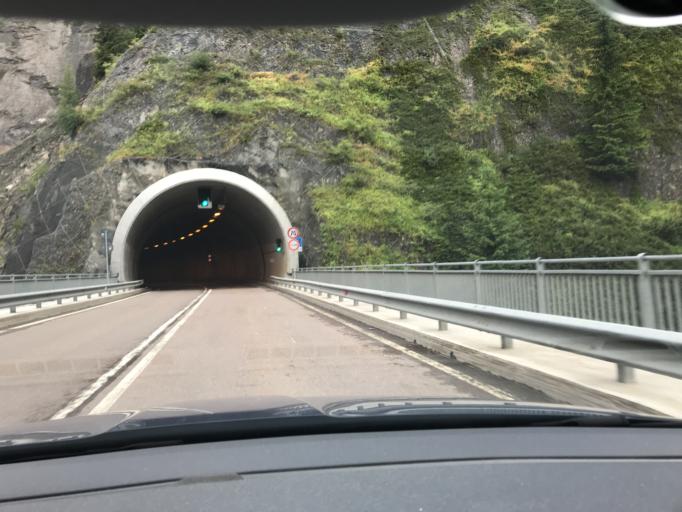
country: IT
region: Trentino-Alto Adige
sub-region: Bolzano
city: Badia
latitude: 46.6201
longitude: 11.8948
